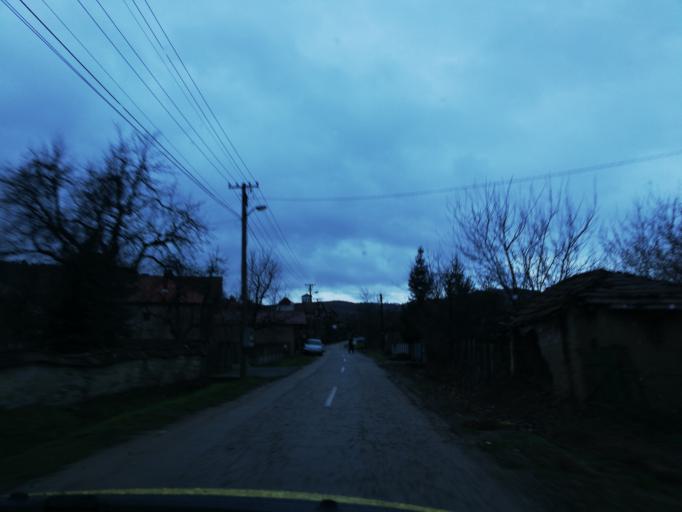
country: RS
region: Central Serbia
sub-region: Pirotski Okrug
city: Dimitrovgrad
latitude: 43.0146
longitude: 22.7295
